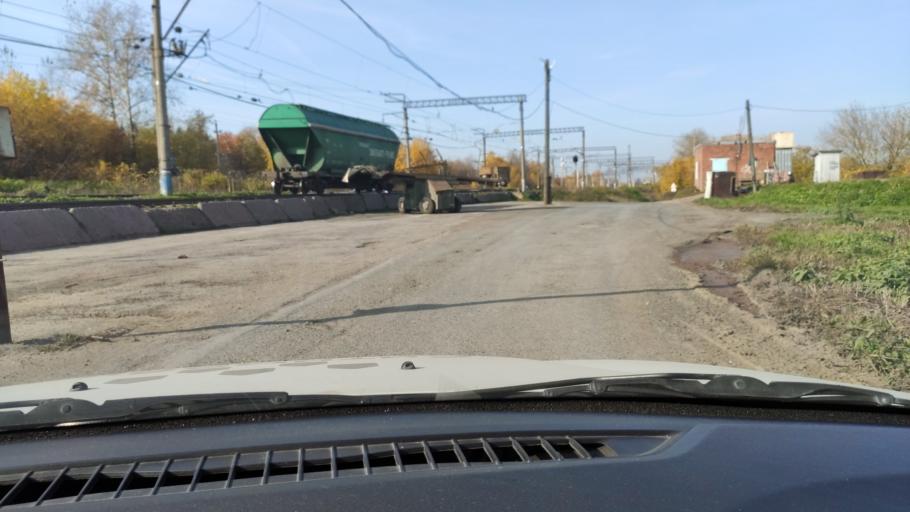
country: RU
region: Perm
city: Sylva
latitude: 58.0423
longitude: 56.7494
